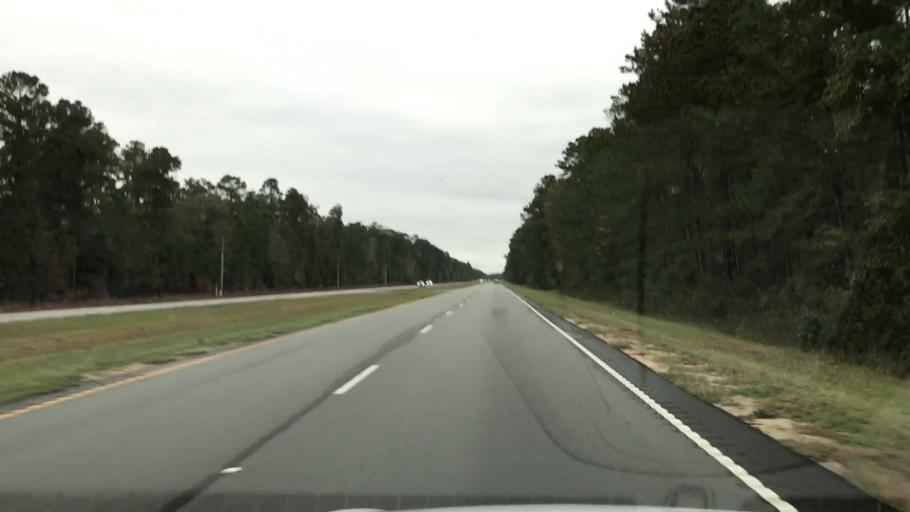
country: US
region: South Carolina
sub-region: Georgetown County
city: Georgetown
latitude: 33.2549
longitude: -79.3717
